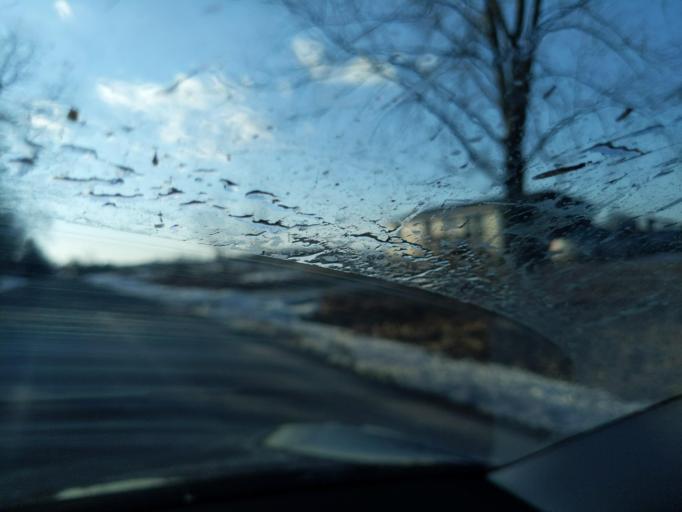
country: US
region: Michigan
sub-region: Ingham County
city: Stockbridge
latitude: 42.5184
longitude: -84.1824
